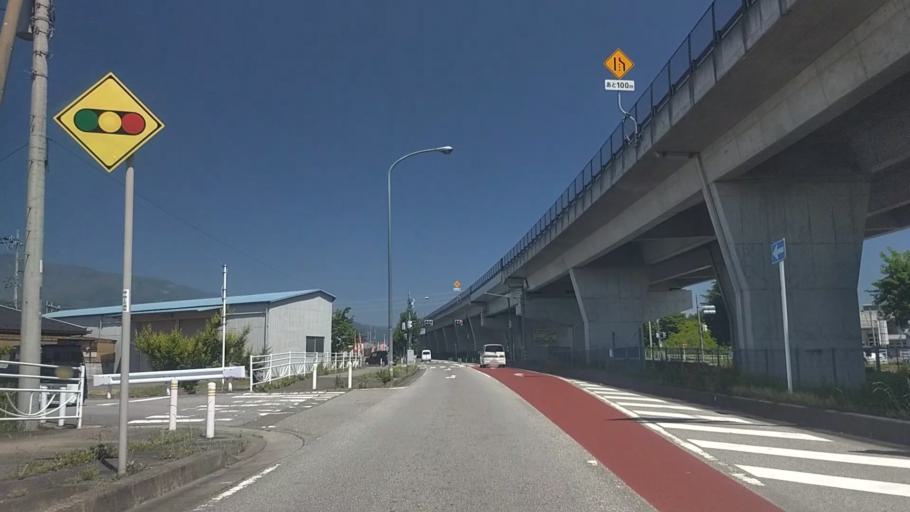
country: JP
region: Yamanashi
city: Ryuo
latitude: 35.6192
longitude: 138.4785
